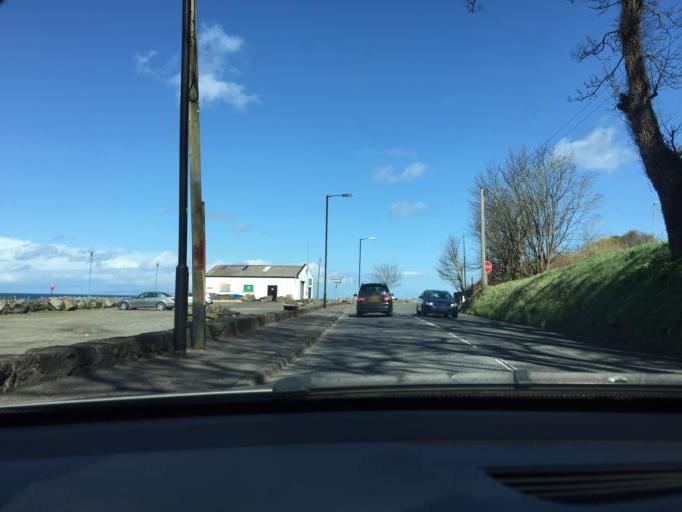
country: GB
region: Northern Ireland
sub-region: Larne District
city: Carnlough
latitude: 54.9687
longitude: -5.9503
